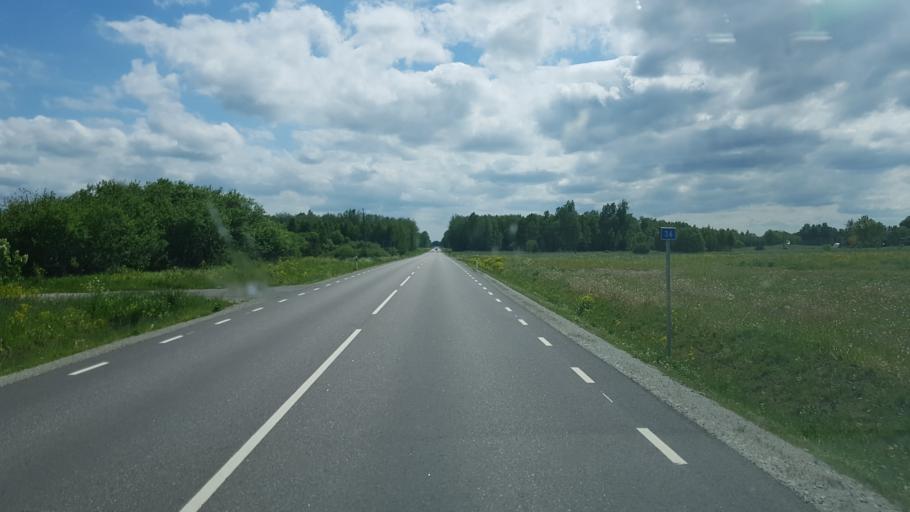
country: EE
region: Laeaene-Virumaa
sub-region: Vinni vald
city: Vinni
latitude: 59.1003
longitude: 26.6203
